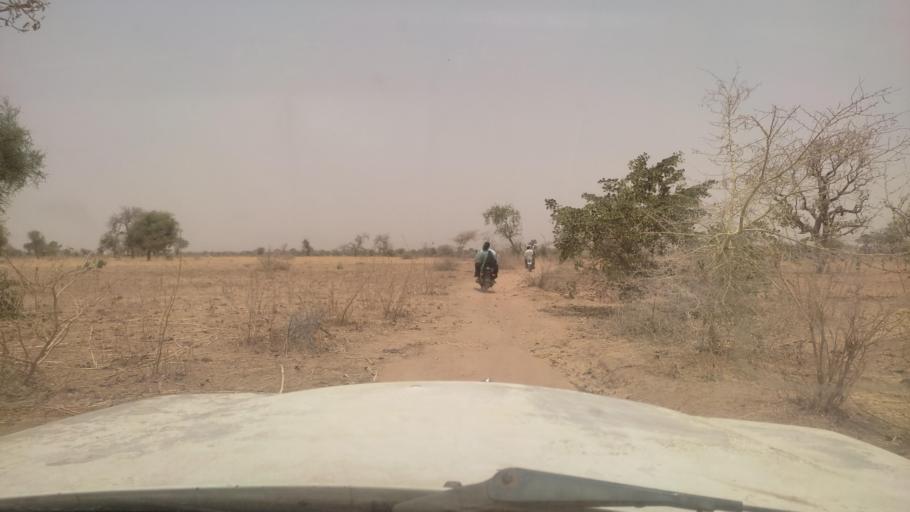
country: BF
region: Est
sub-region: Gnagna Province
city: Bogande
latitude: 13.0330
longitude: -0.0747
